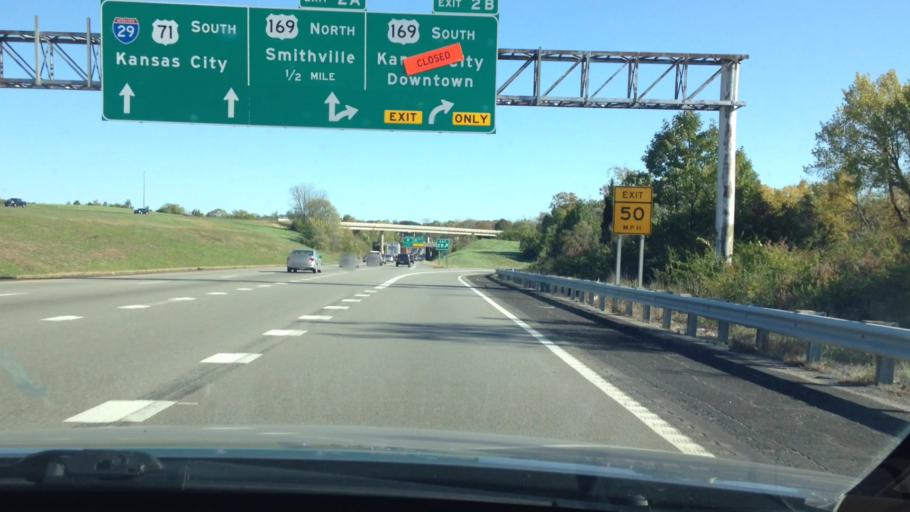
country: US
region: Missouri
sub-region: Platte County
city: Riverside
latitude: 39.1851
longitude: -94.5969
